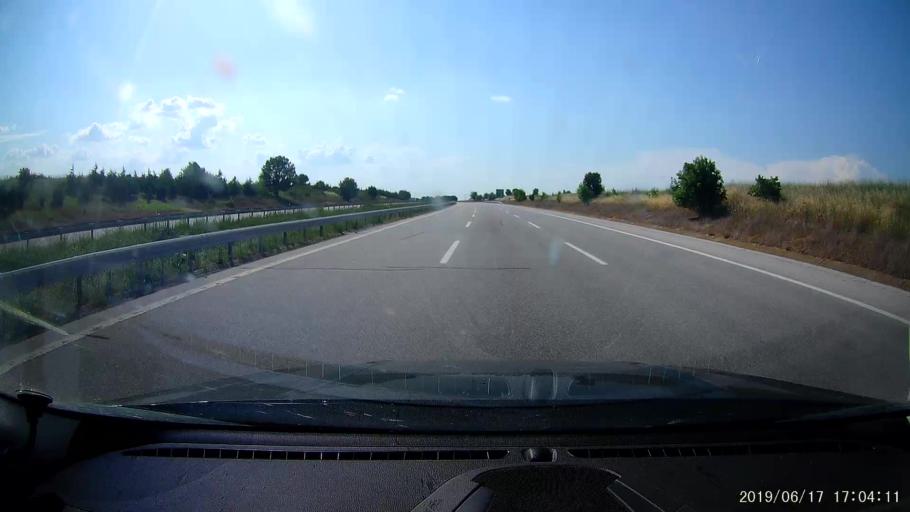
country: TR
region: Edirne
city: Haskoy
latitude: 41.6522
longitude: 26.7343
